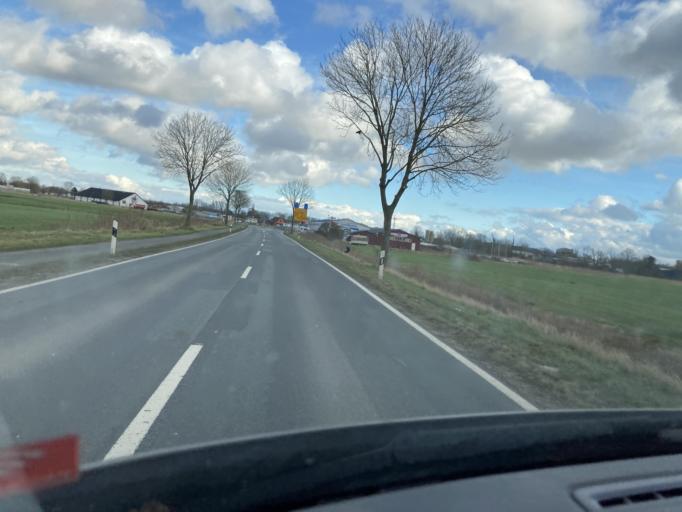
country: DE
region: Lower Saxony
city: Sande
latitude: 53.4901
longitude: 8.0201
